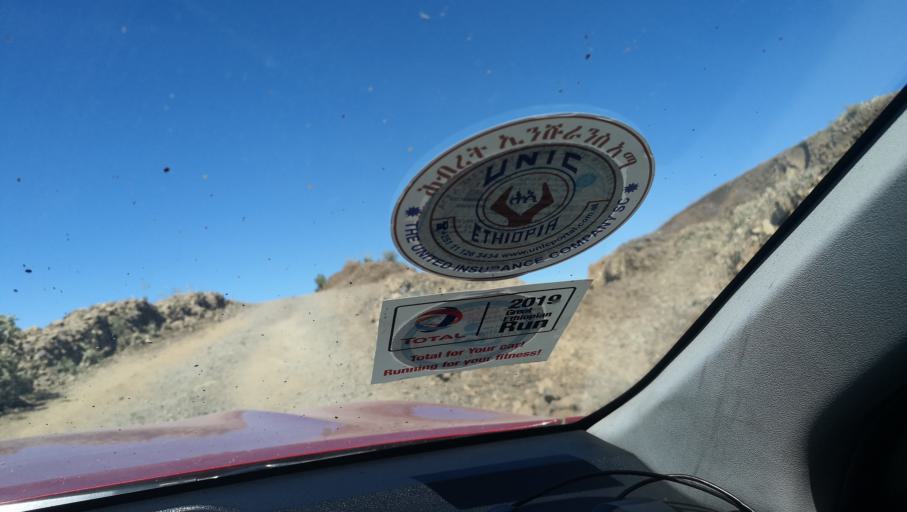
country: ET
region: Amhara
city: Debre Tabor
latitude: 11.5591
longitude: 38.1413
